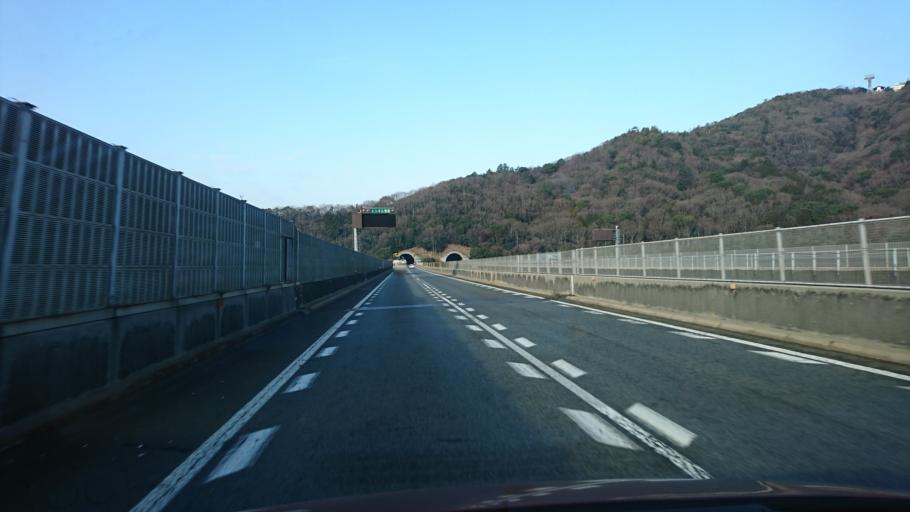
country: JP
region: Hyogo
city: Himeji
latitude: 34.8778
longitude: 134.6681
